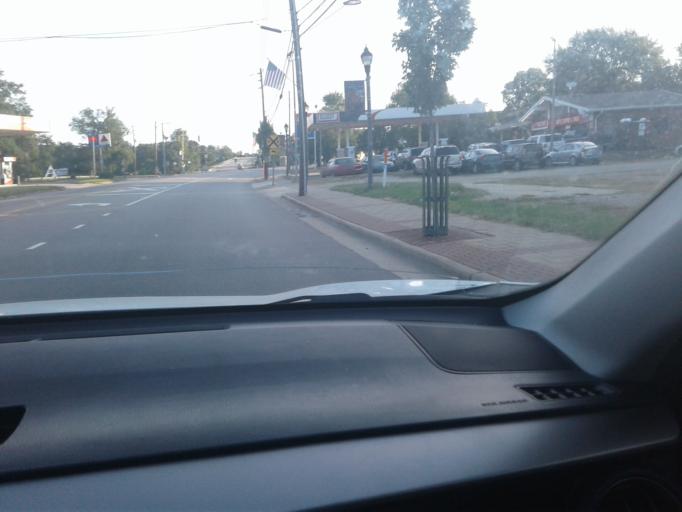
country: US
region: North Carolina
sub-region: Wake County
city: Fuquay-Varina
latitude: 35.5878
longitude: -78.7998
